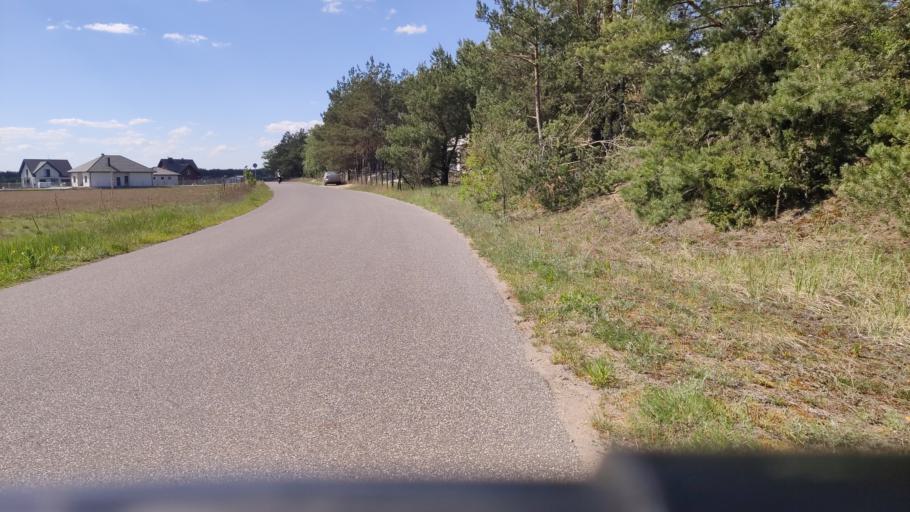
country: PL
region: Kujawsko-Pomorskie
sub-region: Wloclawek
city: Wloclawek
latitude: 52.5835
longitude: 19.0955
